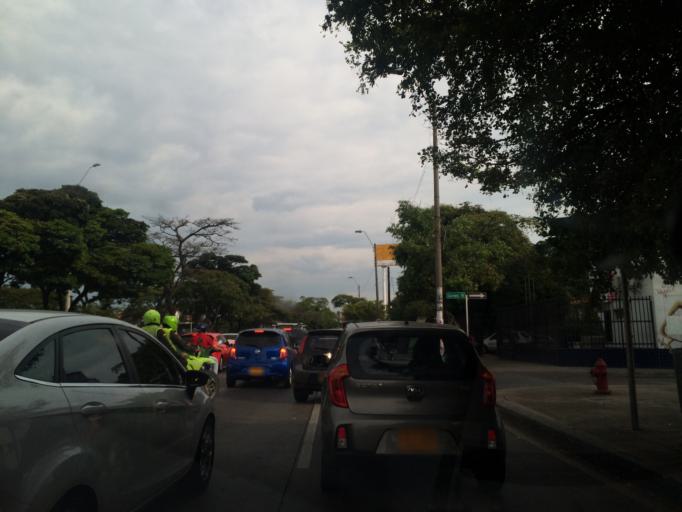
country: CO
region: Valle del Cauca
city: Cali
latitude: 3.3894
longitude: -76.5453
